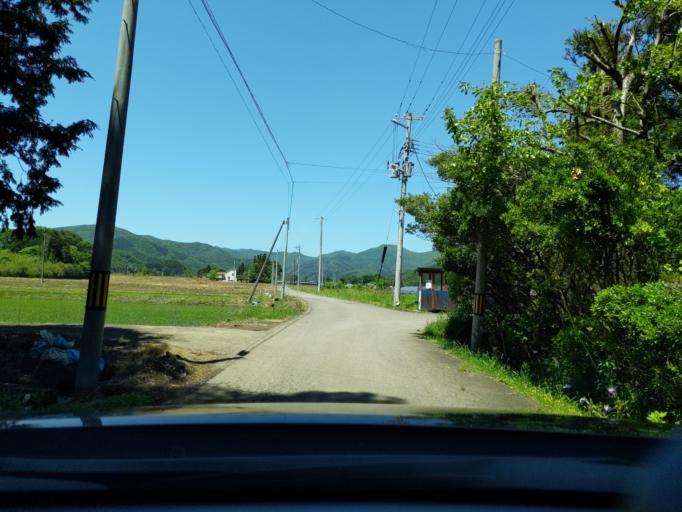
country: JP
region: Fukushima
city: Koriyama
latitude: 37.4046
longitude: 140.2674
